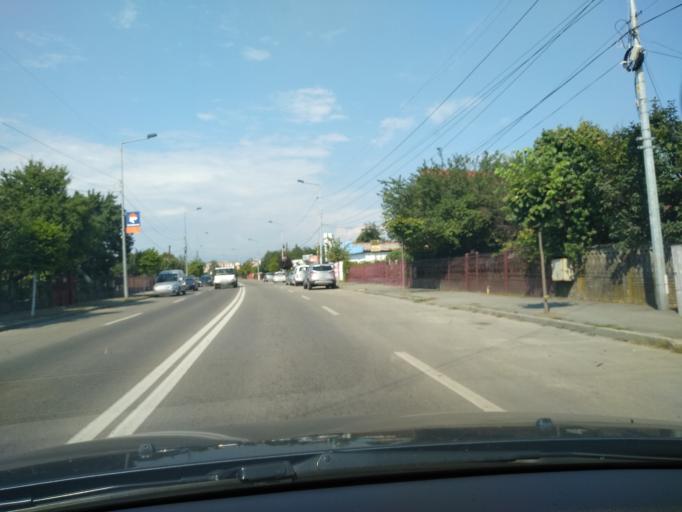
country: RO
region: Gorj
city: Targu Jiu
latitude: 45.0180
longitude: 23.2679
